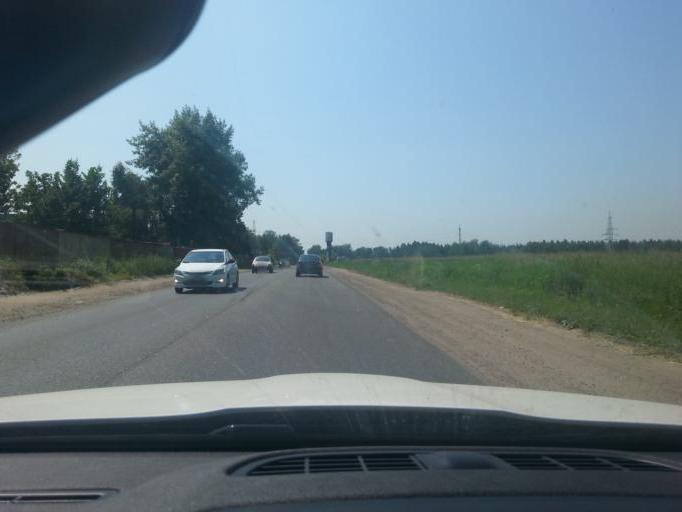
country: RU
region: Moskovskaya
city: Zheleznodorozhnyy
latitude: 55.7237
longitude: 37.9756
